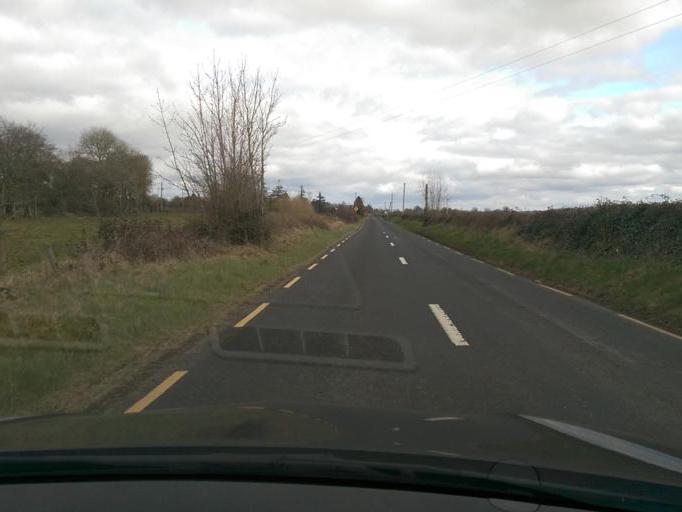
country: IE
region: Connaught
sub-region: County Galway
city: Ballinasloe
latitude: 53.3316
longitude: -8.3610
